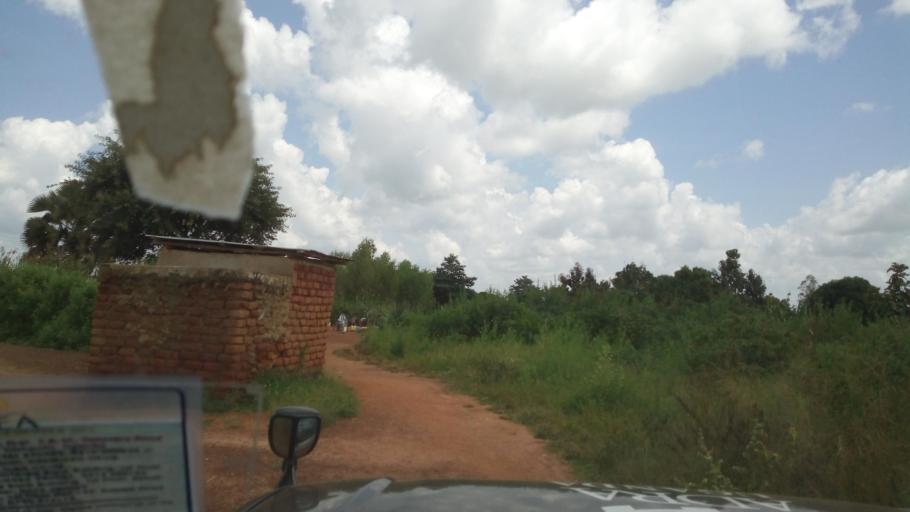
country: UG
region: Northern Region
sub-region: Yumbe District
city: Yumbe
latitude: 3.4713
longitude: 31.2522
